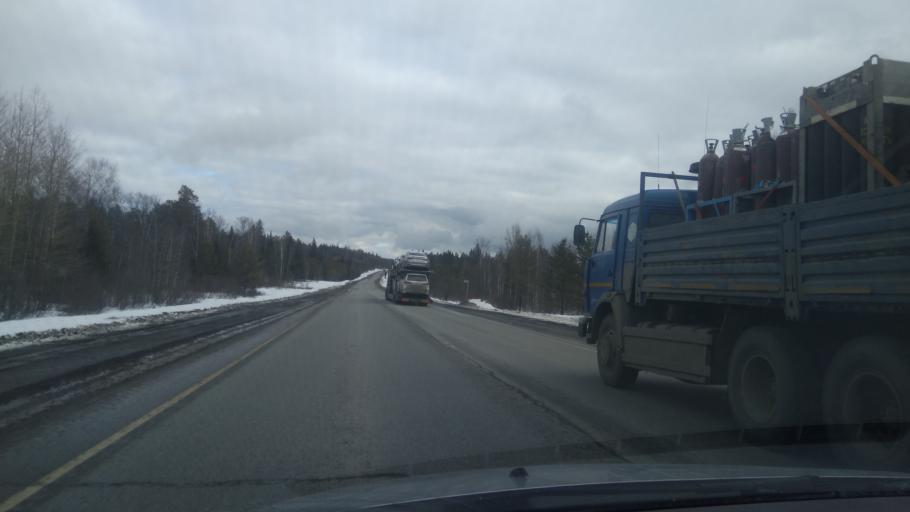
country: RU
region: Sverdlovsk
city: Nizhniye Sergi
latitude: 56.8250
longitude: 59.2587
